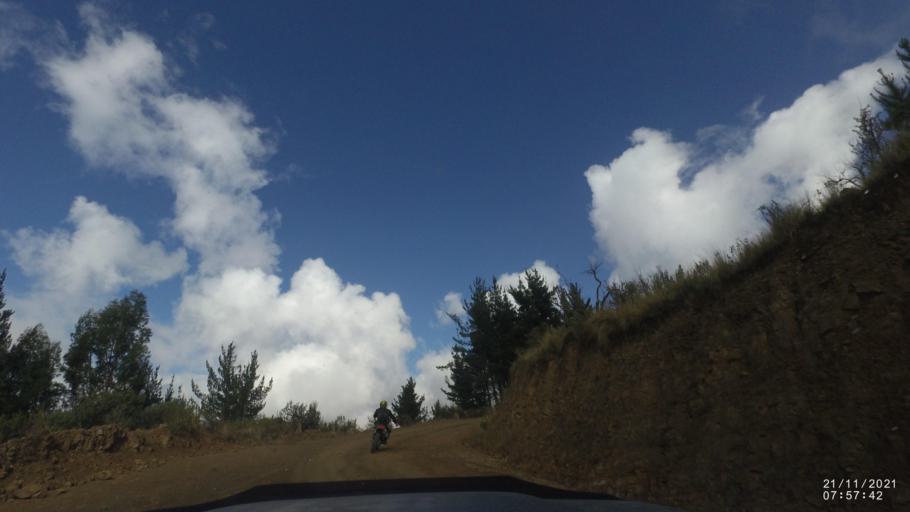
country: BO
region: Cochabamba
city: Cochabamba
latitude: -17.2961
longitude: -66.2193
